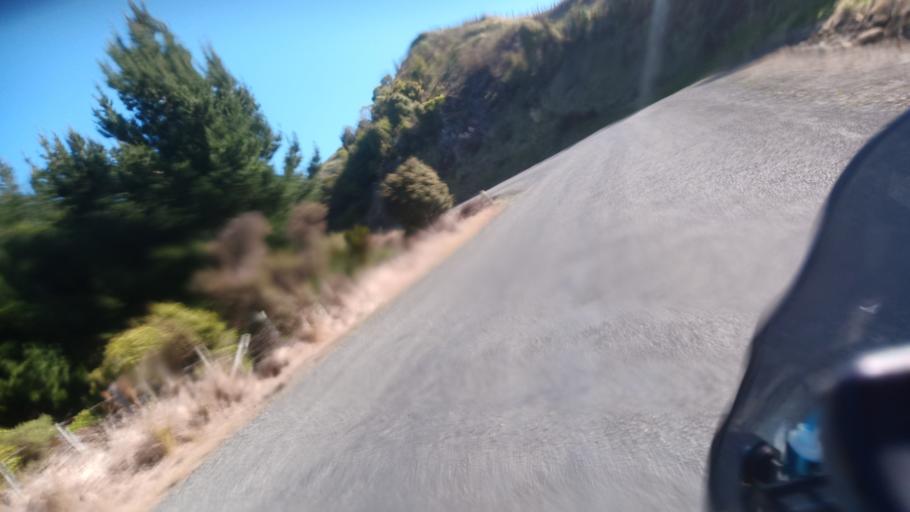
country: NZ
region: Gisborne
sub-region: Gisborne District
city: Gisborne
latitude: -39.1559
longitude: 177.9102
